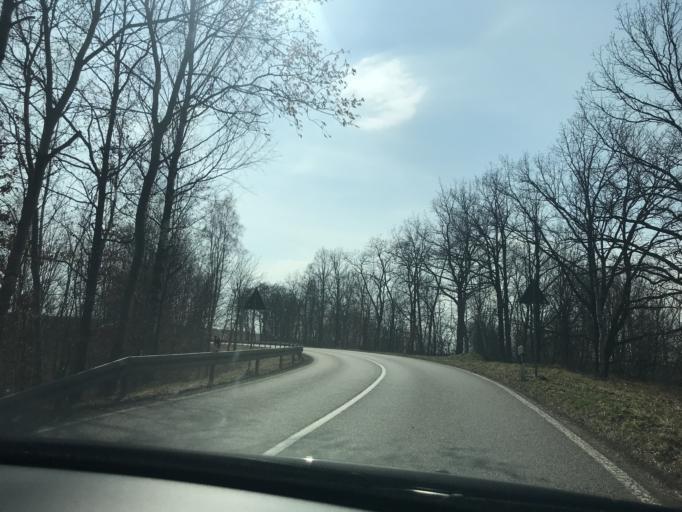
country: DE
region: Saxony
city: Seelitz
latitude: 51.0280
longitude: 12.7994
